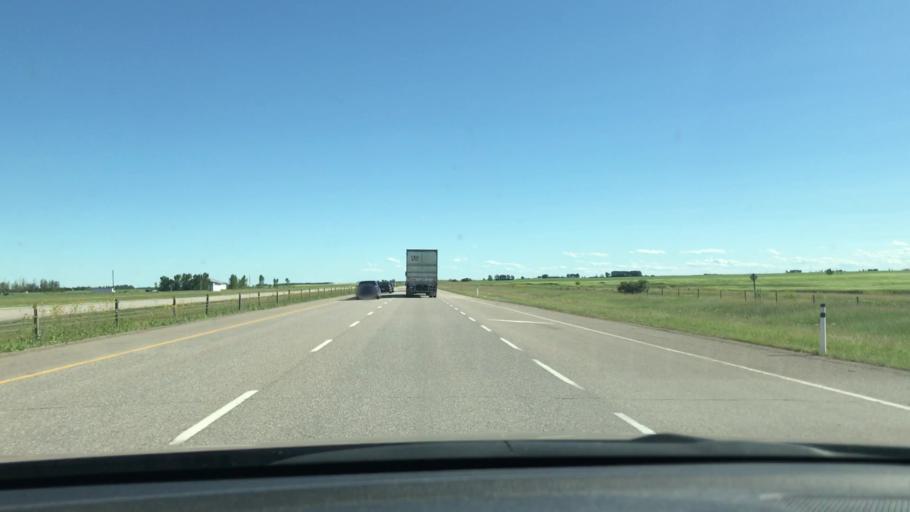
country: CA
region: Alberta
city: Olds
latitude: 51.7062
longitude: -114.0254
